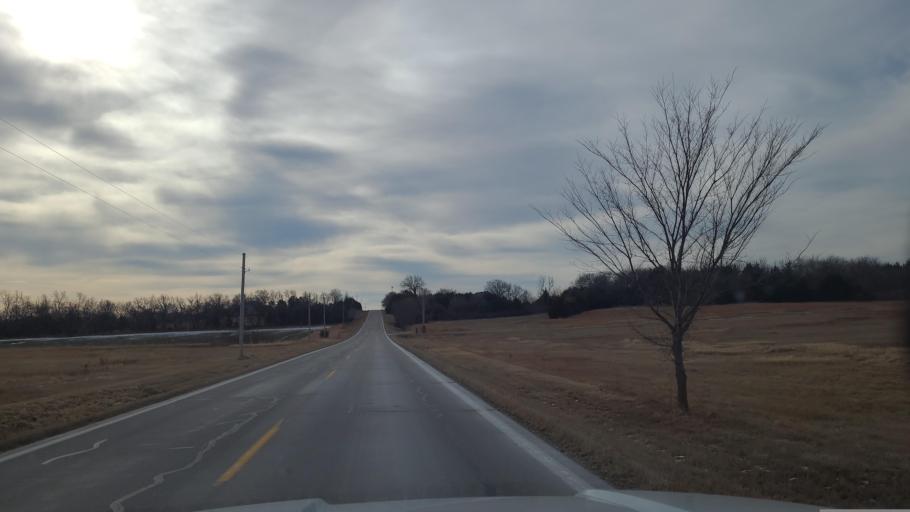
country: US
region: Kansas
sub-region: Douglas County
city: Baldwin City
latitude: 38.8333
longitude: -95.1865
